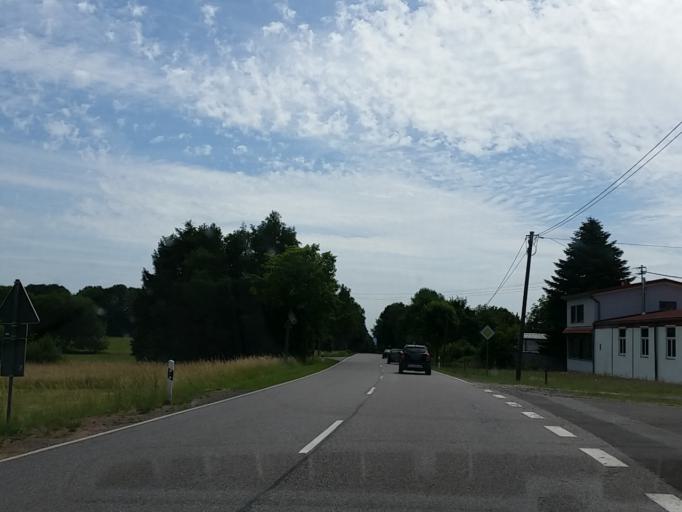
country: DE
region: Saarland
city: Britten
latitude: 49.5287
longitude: 6.6720
